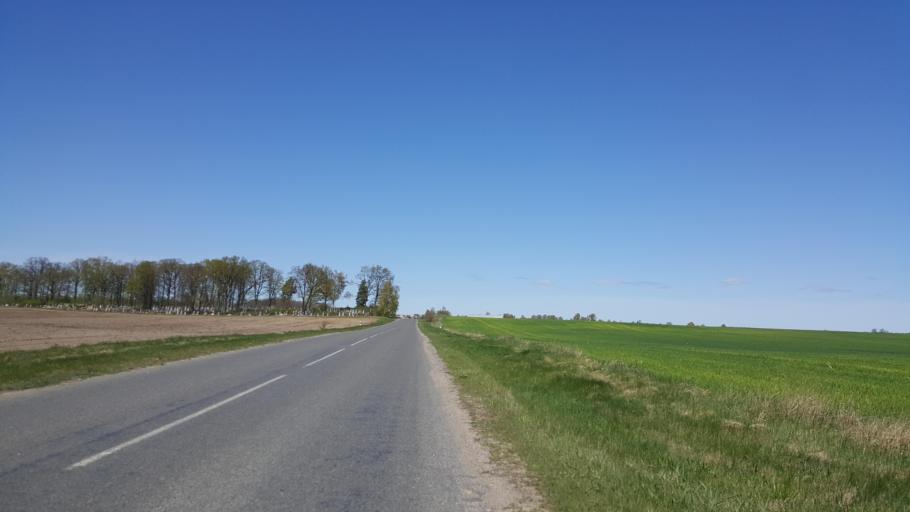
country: BY
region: Brest
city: Charnawchytsy
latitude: 52.3294
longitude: 23.6078
